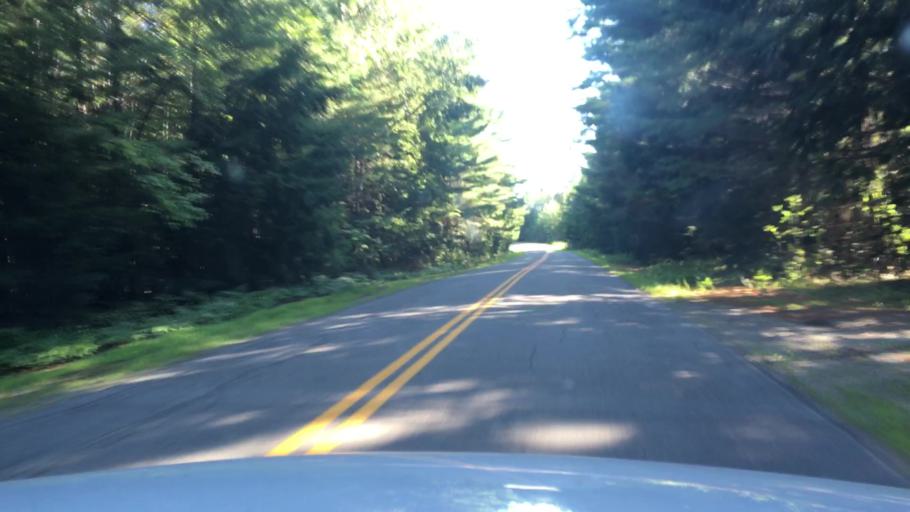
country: US
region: Maine
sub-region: Penobscot County
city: Enfield
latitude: 45.2115
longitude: -68.5892
